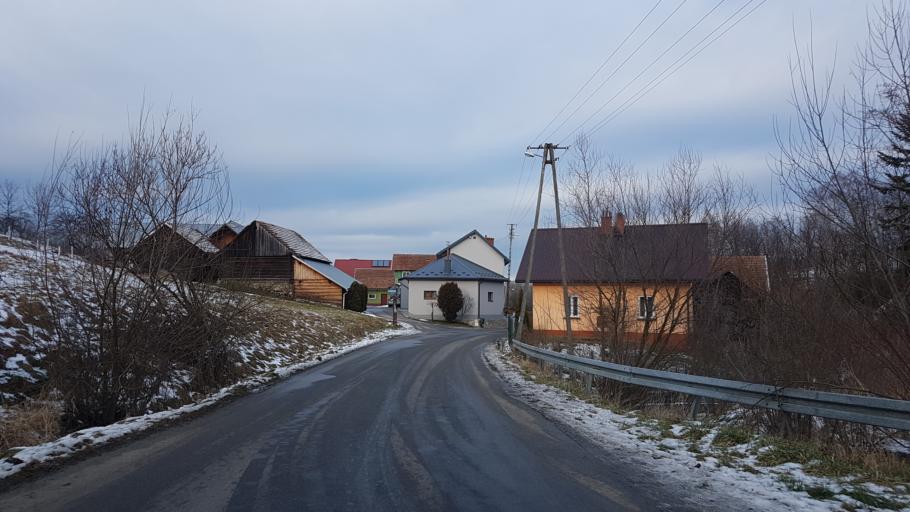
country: PL
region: Lesser Poland Voivodeship
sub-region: Powiat nowosadecki
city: Stary Sacz
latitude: 49.5189
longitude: 20.6080
